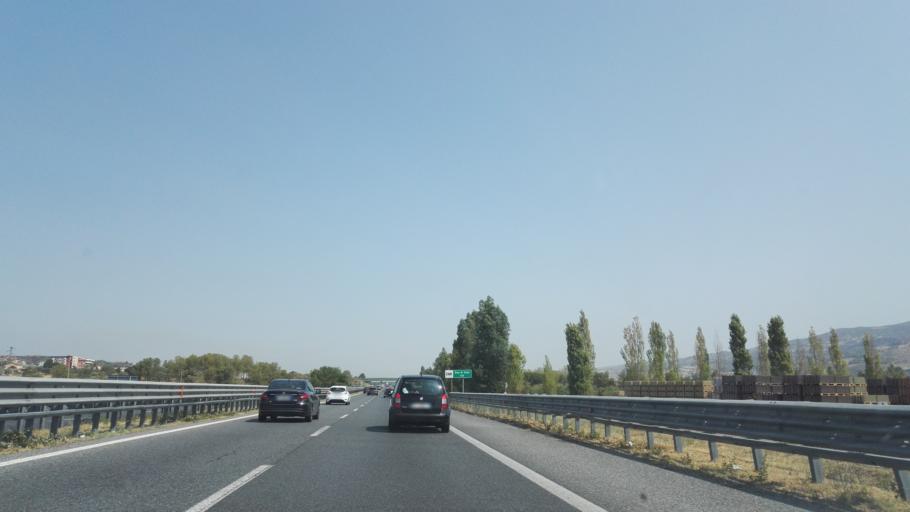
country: IT
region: Calabria
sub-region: Provincia di Cosenza
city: Settimo
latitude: 39.3969
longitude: 16.2431
